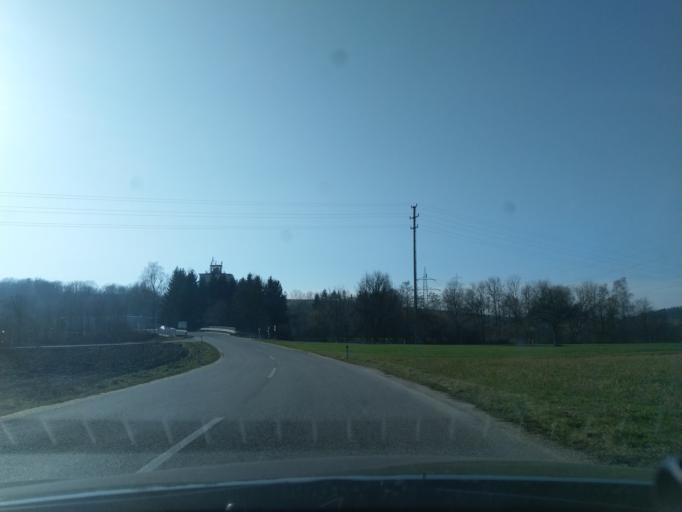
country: AT
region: Upper Austria
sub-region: Politischer Bezirk Ried im Innkreis
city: Ried im Innkreis
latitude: 48.2286
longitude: 13.4752
